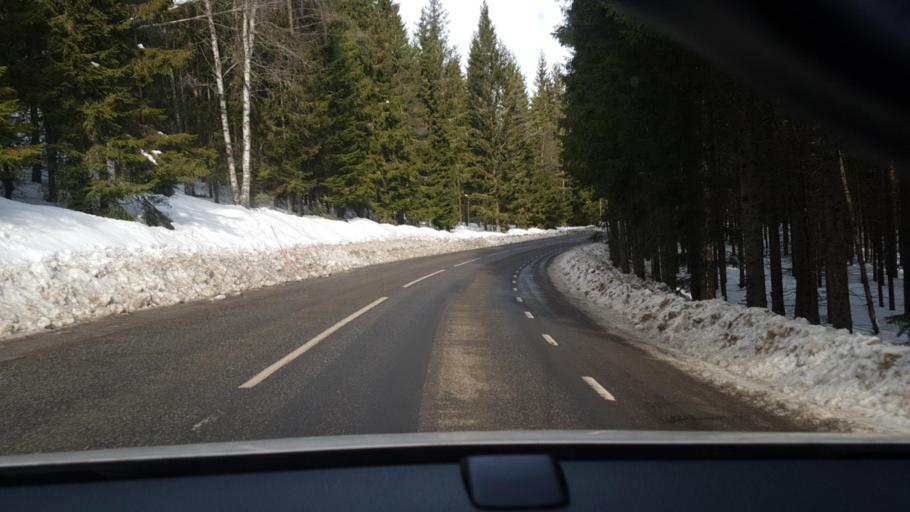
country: SE
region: Vaermland
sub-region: Eda Kommun
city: Amotfors
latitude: 59.6063
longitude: 12.3219
